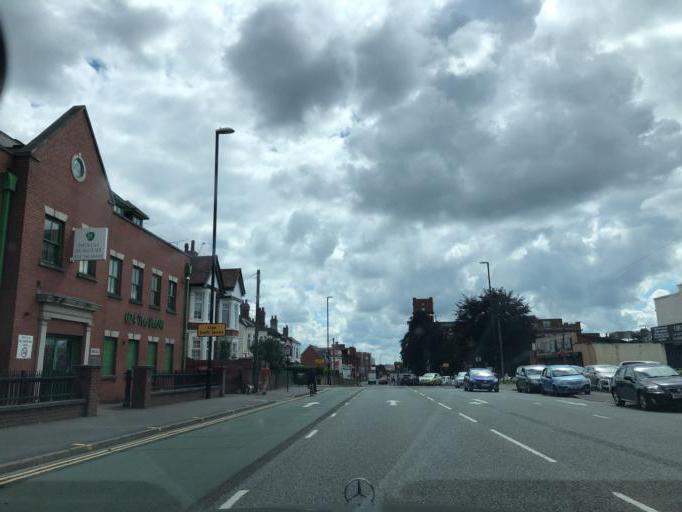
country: GB
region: England
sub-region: Coventry
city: Coventry
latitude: 52.4260
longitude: -1.5013
